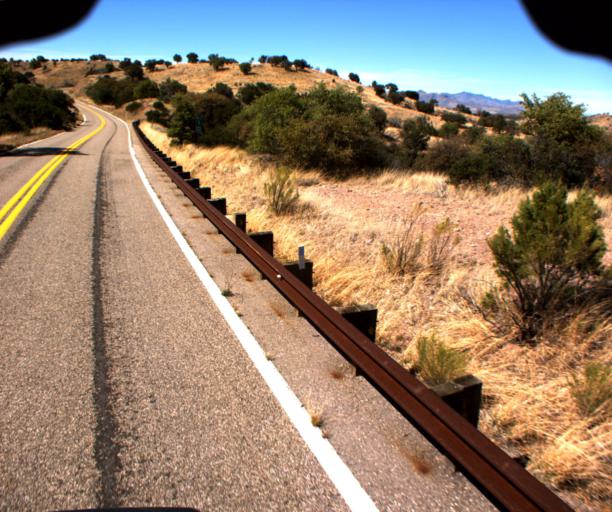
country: US
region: Arizona
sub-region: Cochise County
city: Sierra Vista
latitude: 31.4954
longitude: -110.4928
